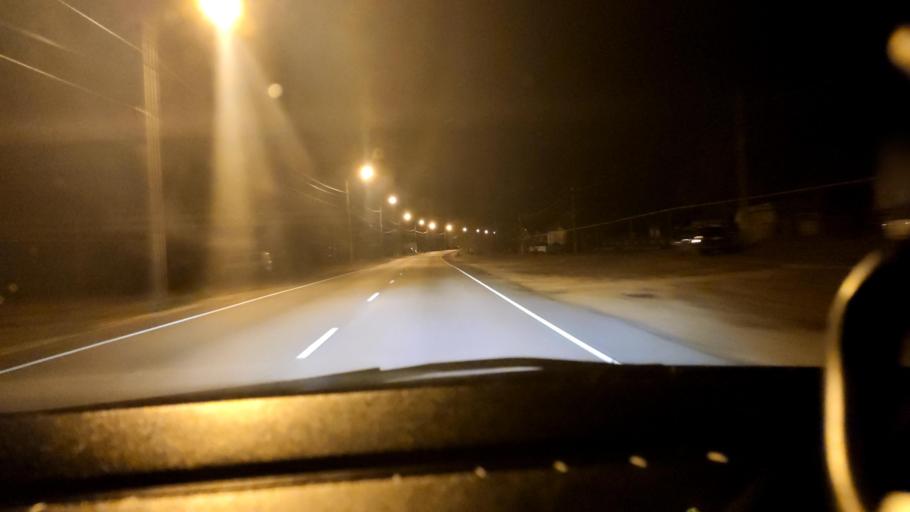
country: RU
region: Voronezj
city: Shilovo
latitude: 51.5547
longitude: 39.0648
